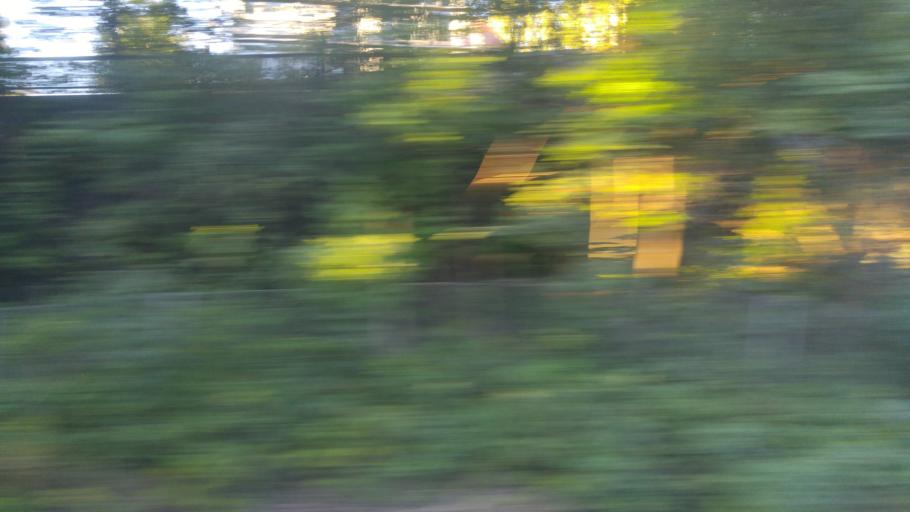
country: NO
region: Akershus
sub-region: Lorenskog
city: Kjenn
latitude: 59.9469
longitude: 10.9363
